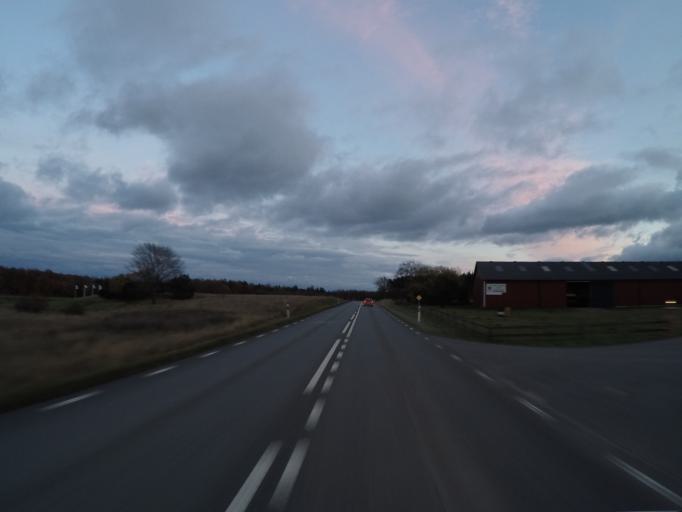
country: SE
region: Skane
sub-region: Kristianstads Kommun
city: Degeberga
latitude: 55.8189
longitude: 14.1248
